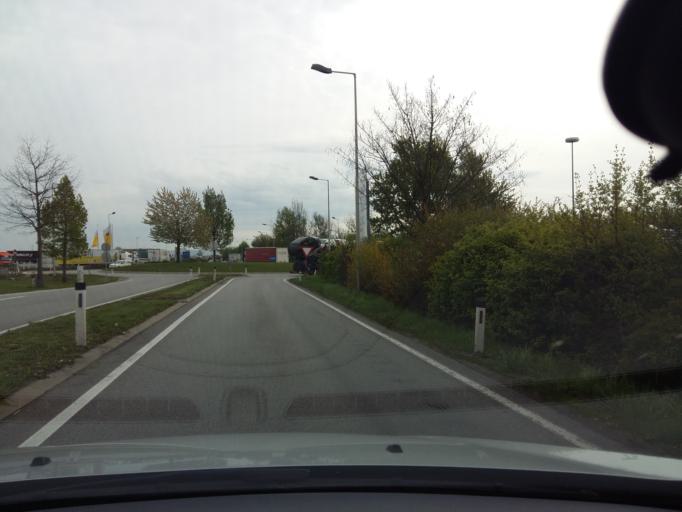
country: AT
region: Upper Austria
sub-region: Politischer Bezirk Scharding
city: Sankt Marienkirchen bei Schaerding
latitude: 48.3920
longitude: 13.4264
